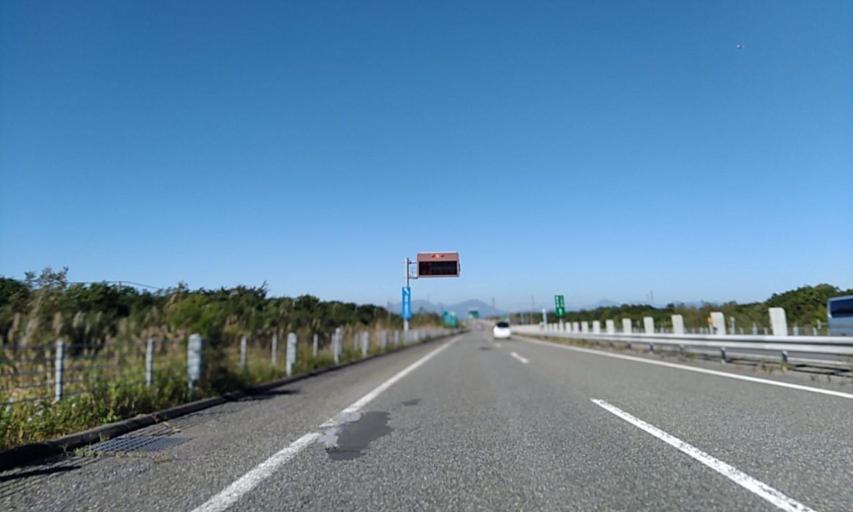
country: JP
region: Hokkaido
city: Tomakomai
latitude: 42.6740
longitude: 141.7414
